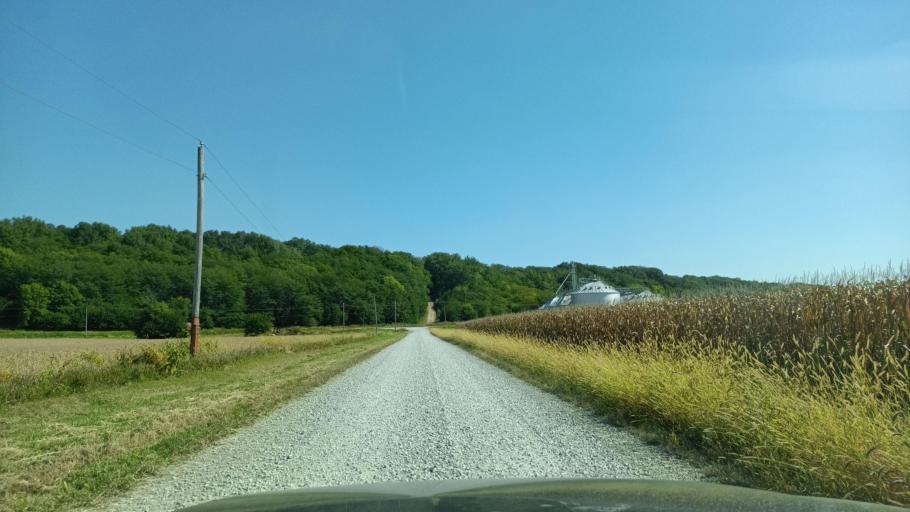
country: US
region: Illinois
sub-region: Mercer County
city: Aledo
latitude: 41.1645
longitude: -90.9158
